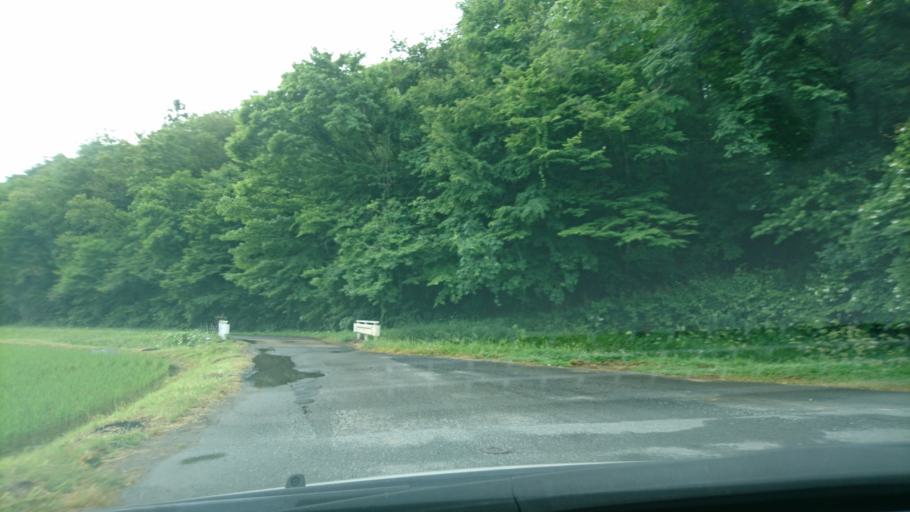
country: JP
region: Iwate
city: Ichinoseki
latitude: 38.8961
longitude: 141.1495
